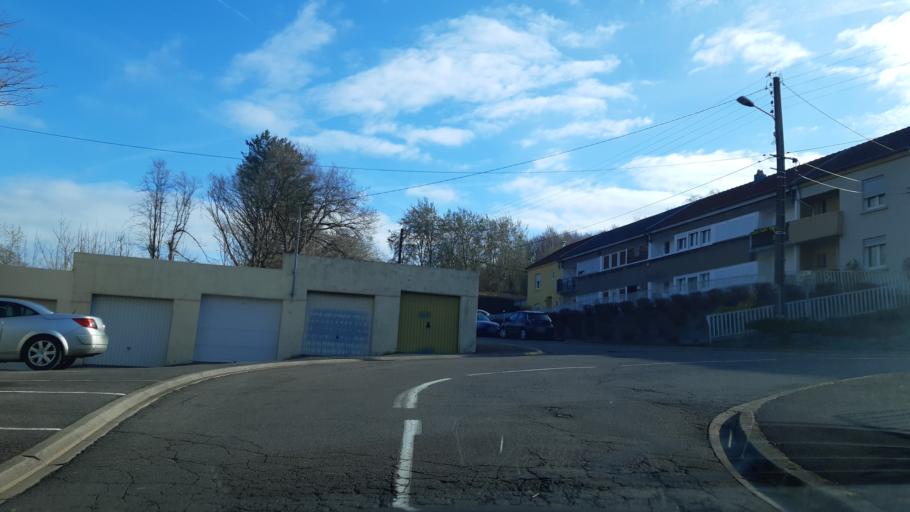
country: FR
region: Lorraine
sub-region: Departement de la Moselle
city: Audun-le-Tiche
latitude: 49.4802
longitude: 5.9669
